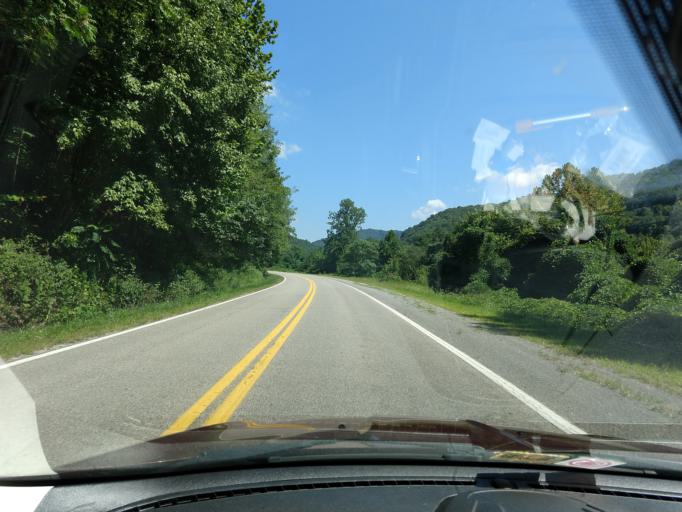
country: US
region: West Virginia
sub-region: Kanawha County
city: Montgomery
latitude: 38.1262
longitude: -81.2217
